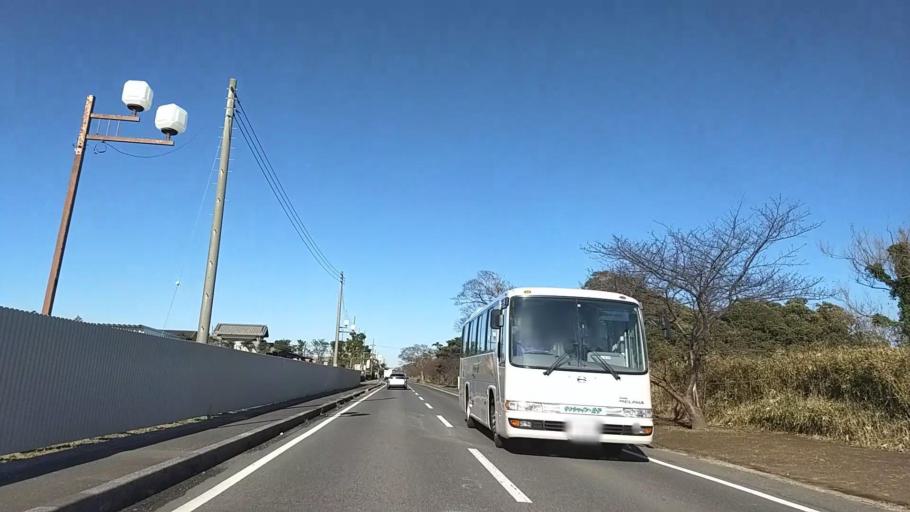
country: JP
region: Chiba
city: Mobara
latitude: 35.4220
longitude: 140.3934
